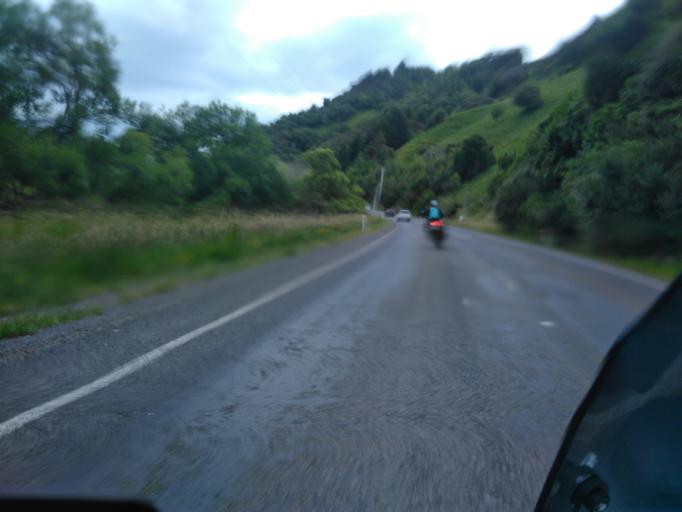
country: NZ
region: Bay of Plenty
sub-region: Opotiki District
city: Opotiki
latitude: -38.3742
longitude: 177.4867
